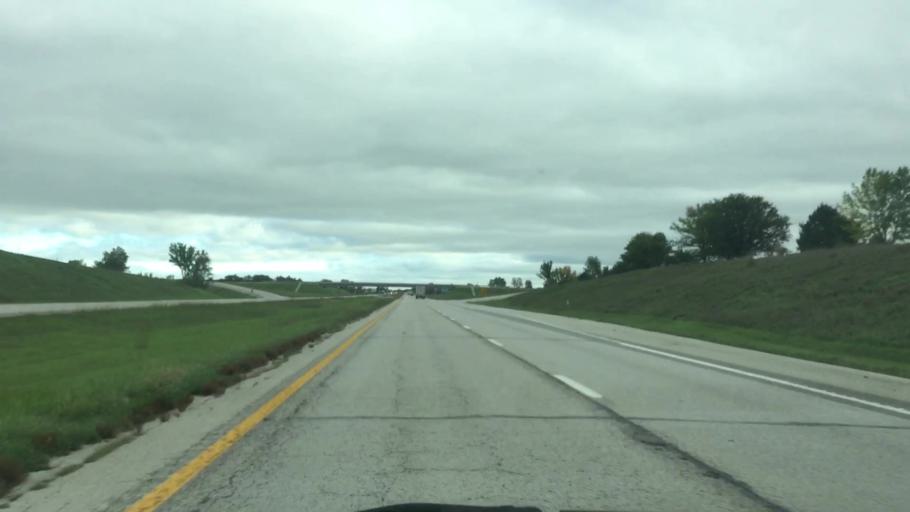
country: US
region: Missouri
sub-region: Harrison County
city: Bethany
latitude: 40.1510
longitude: -94.0358
